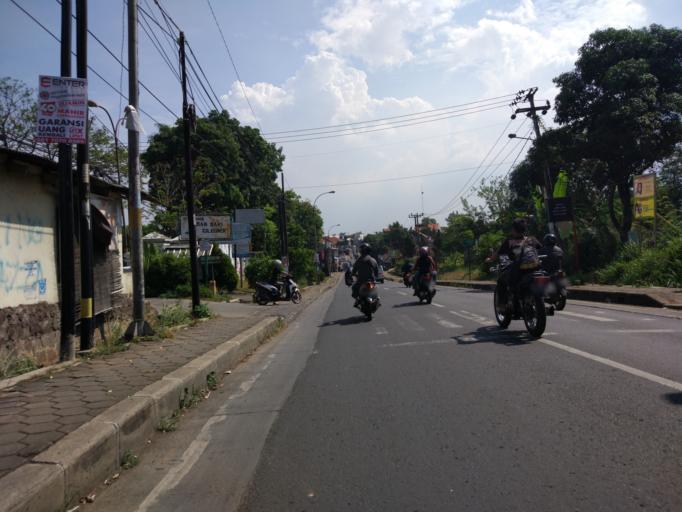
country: ID
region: West Java
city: Cileunyi
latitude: -6.9408
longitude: 107.7441
